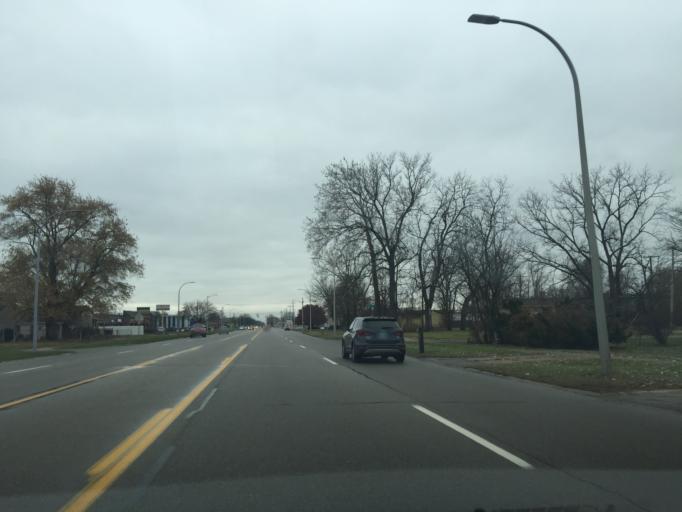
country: US
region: Michigan
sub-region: Oakland County
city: Farmington
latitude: 42.4341
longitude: -83.3363
